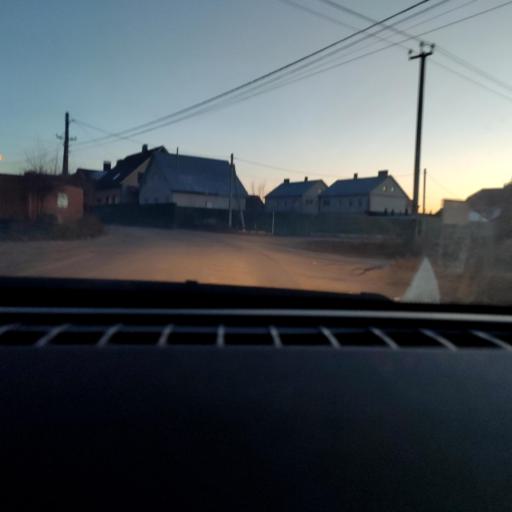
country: RU
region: Voronezj
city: Podgornoye
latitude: 51.7448
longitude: 39.1613
